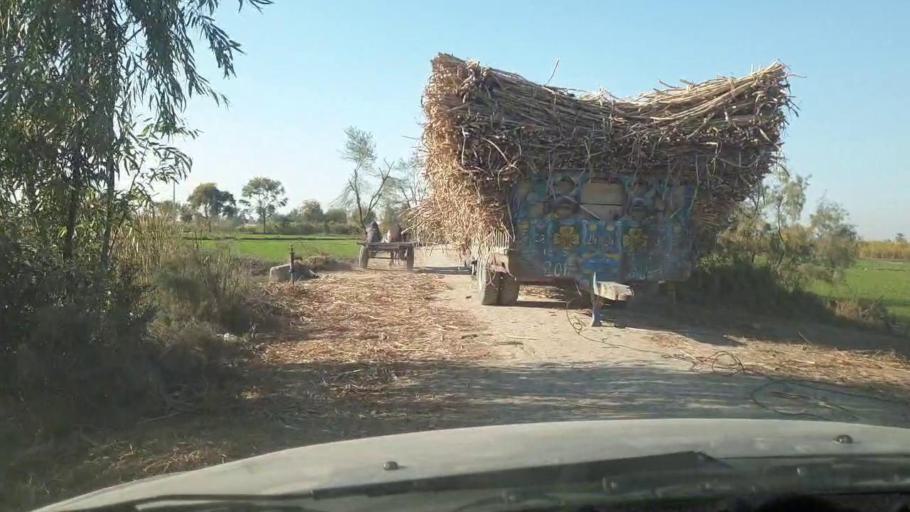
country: PK
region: Sindh
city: Ghotki
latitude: 28.0440
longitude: 69.2941
